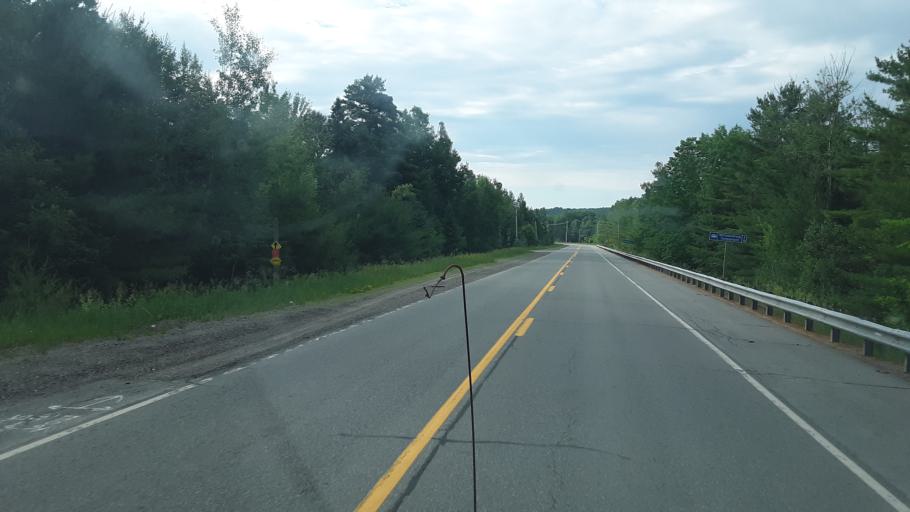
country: US
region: Maine
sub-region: Penobscot County
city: Medway
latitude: 45.6051
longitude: -68.5208
